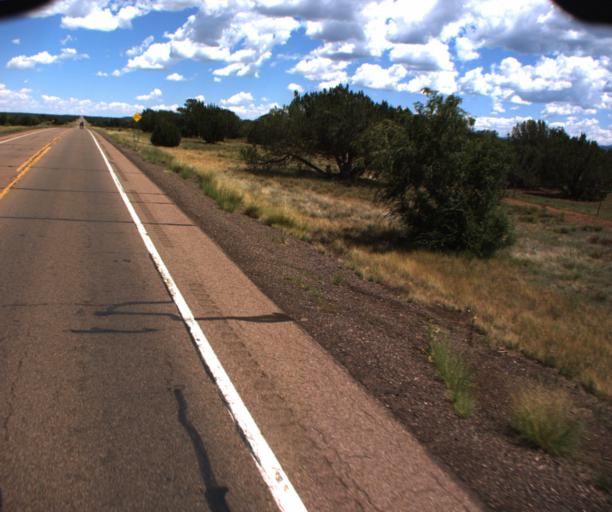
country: US
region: Arizona
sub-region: Navajo County
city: Show Low
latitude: 34.2667
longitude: -109.9470
